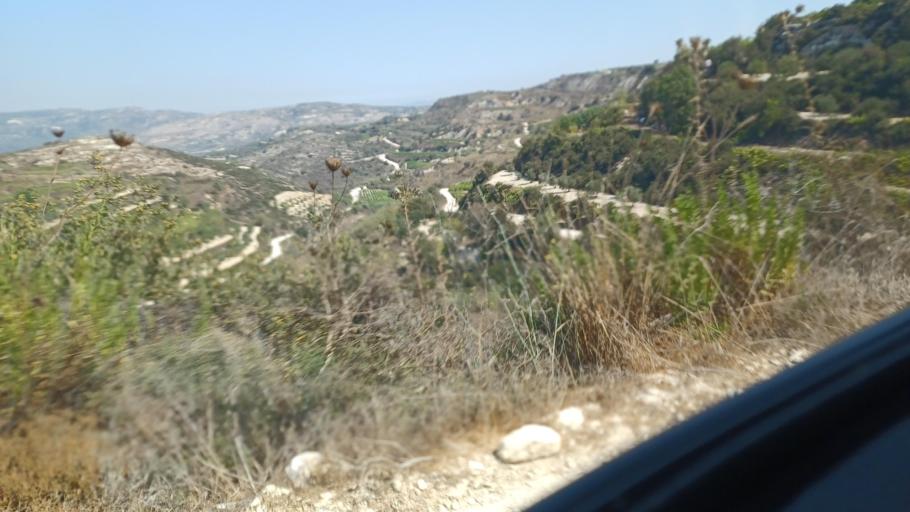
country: CY
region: Pafos
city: Mesogi
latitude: 34.8496
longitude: 32.4688
